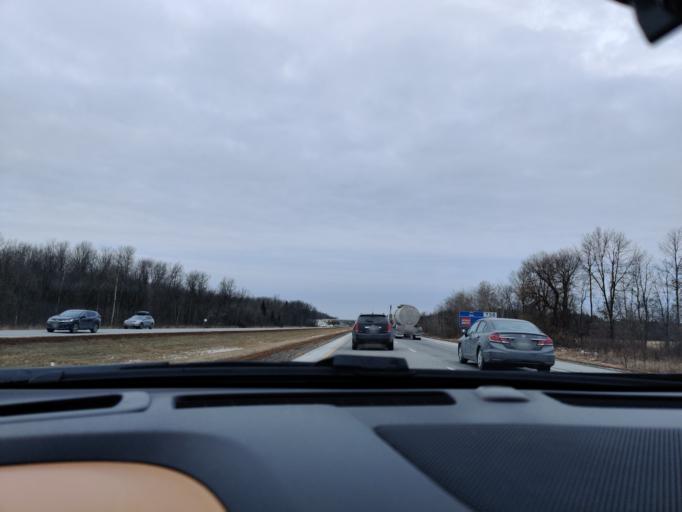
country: US
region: New York
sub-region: St. Lawrence County
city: Ogdensburg
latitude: 44.8733
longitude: -75.2999
